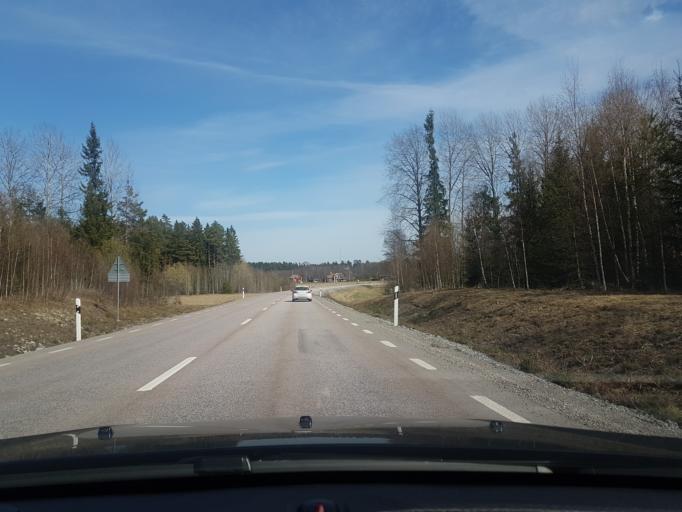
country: SE
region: Vaestmanland
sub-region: Sala Kommun
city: Sala
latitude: 59.9842
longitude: 16.4610
